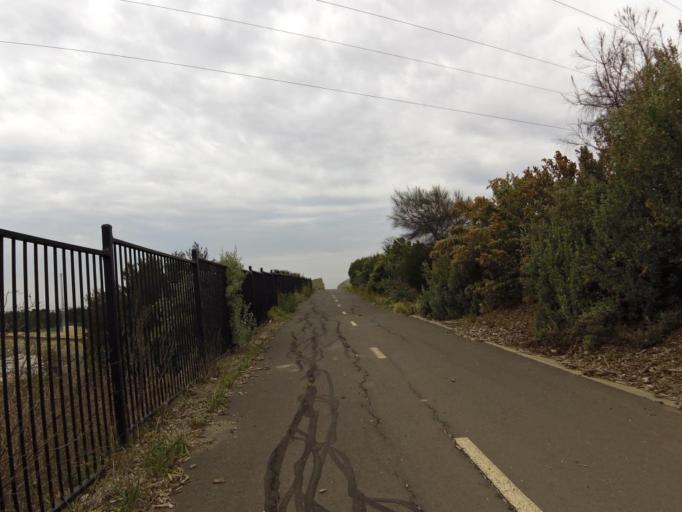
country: AU
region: Victoria
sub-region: Melton
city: Caroline Springs
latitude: -37.7695
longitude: 144.7456
